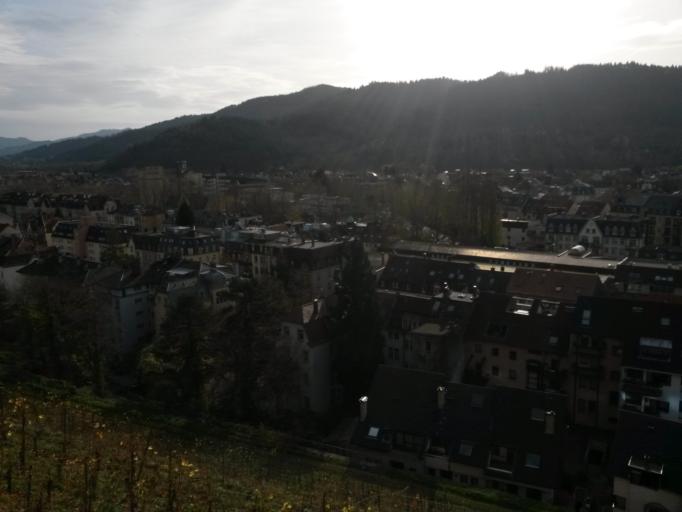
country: DE
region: Baden-Wuerttemberg
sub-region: Freiburg Region
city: Freiburg
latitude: 47.9927
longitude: 7.8558
